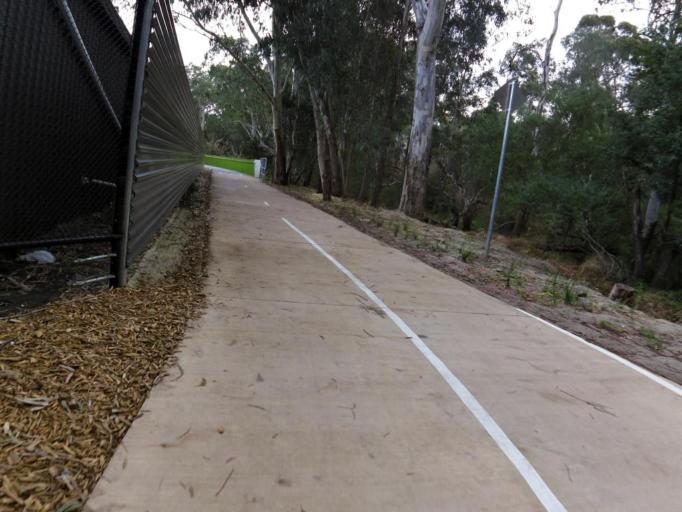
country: AU
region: Victoria
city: Alphington
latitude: -37.7842
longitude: 145.0397
